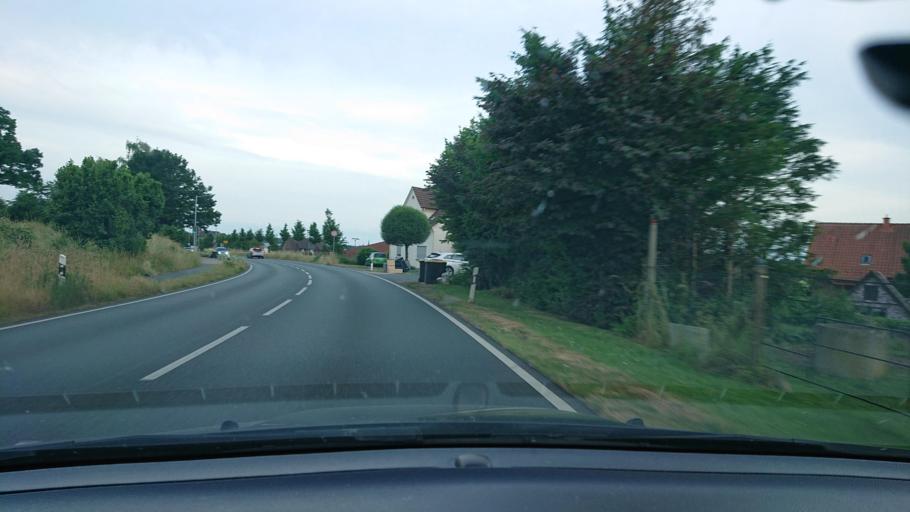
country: DE
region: North Rhine-Westphalia
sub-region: Regierungsbezirk Detmold
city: Herford
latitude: 52.1400
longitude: 8.6492
